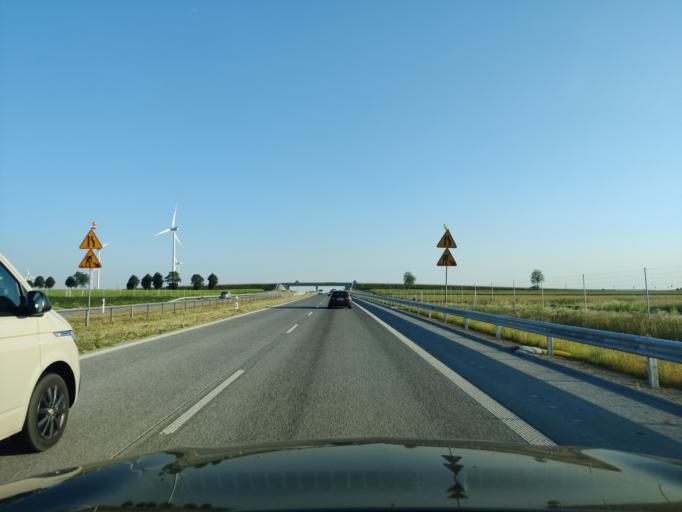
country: PL
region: Masovian Voivodeship
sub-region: Powiat mlawski
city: Wisniewo
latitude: 53.0645
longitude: 20.3666
